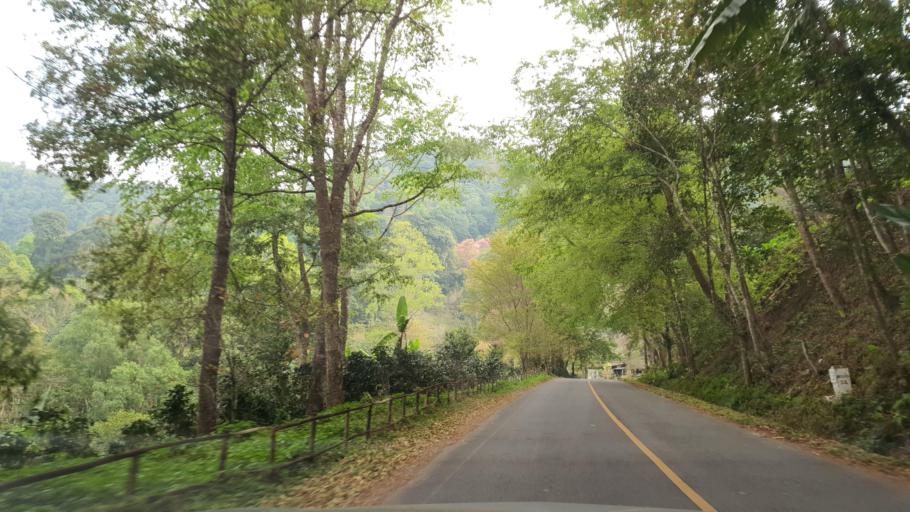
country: TH
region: Chiang Mai
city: Mae On
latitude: 18.9377
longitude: 99.3763
